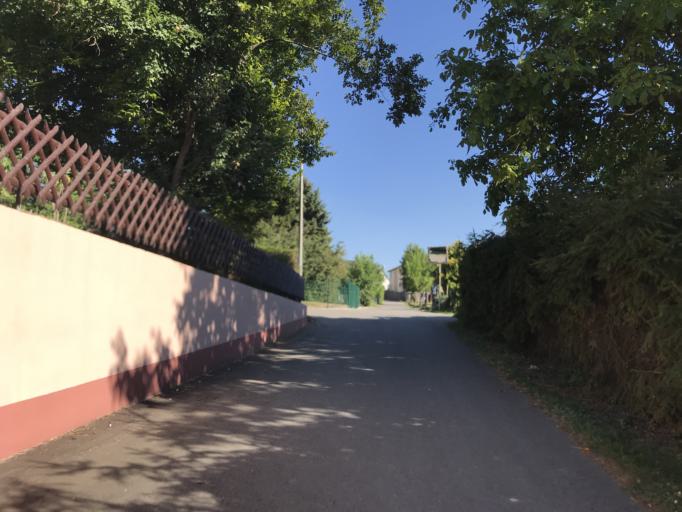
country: DE
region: Rheinland-Pfalz
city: Schwabenheim
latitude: 49.9310
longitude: 8.0915
